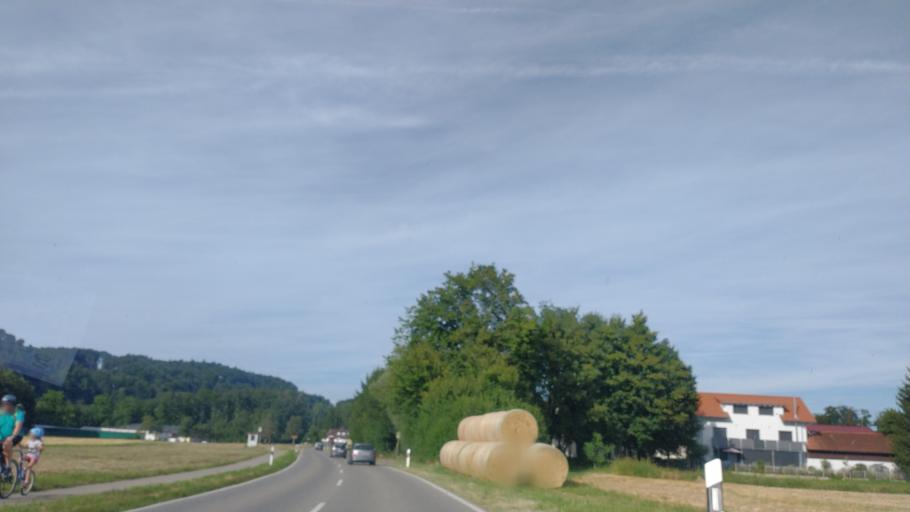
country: DE
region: Baden-Wuerttemberg
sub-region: Tuebingen Region
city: Kressbronn am Bodensee
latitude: 47.6322
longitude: 9.6218
